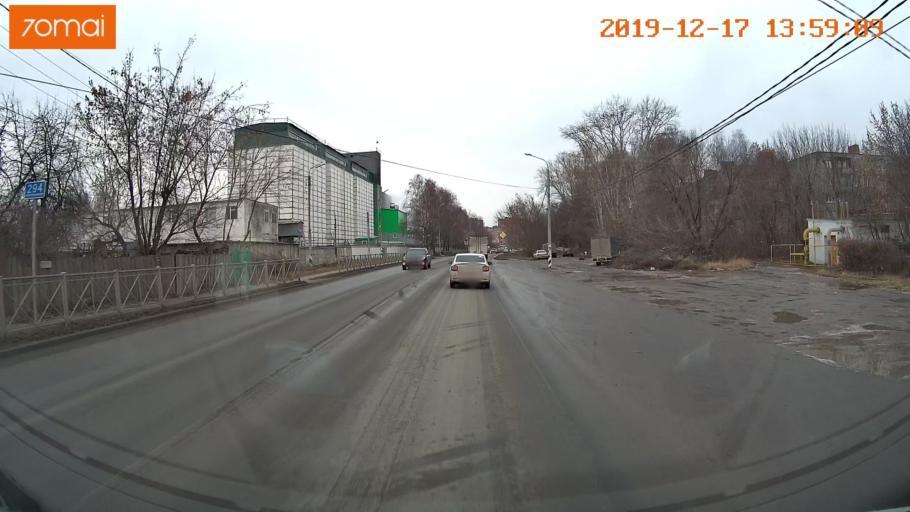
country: RU
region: Rjazan
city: Ryazan'
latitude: 54.6212
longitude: 39.6793
